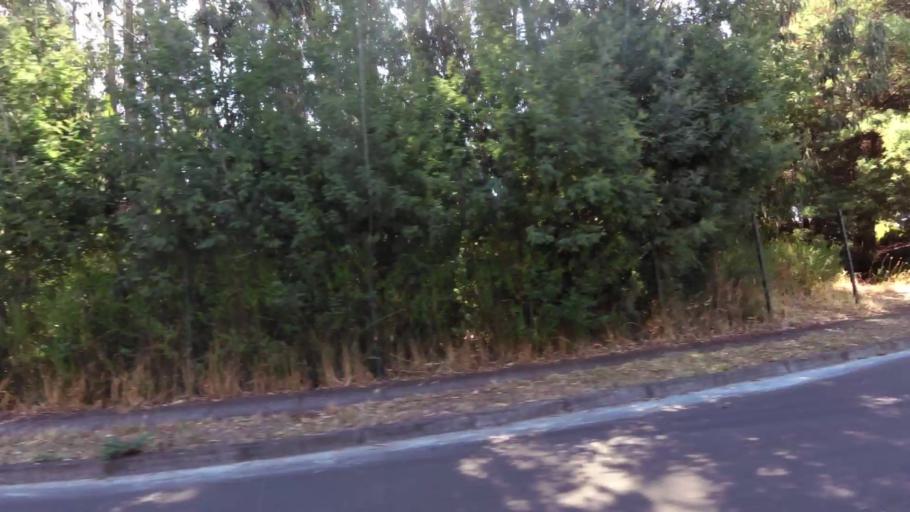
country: CL
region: Biobio
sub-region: Provincia de Concepcion
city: Concepcion
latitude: -36.7835
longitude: -73.0483
